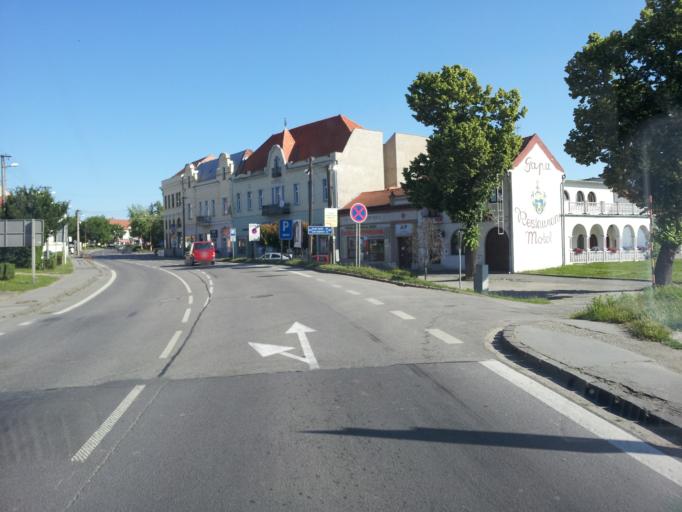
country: SK
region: Nitriansky
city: Sahy
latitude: 48.0682
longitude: 18.9497
